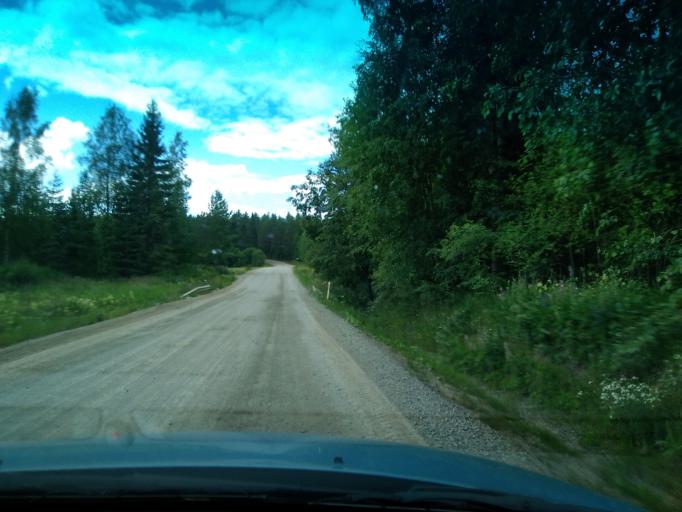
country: FI
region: Central Finland
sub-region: Saarijaervi-Viitasaari
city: Karstula
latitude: 62.8082
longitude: 25.0048
